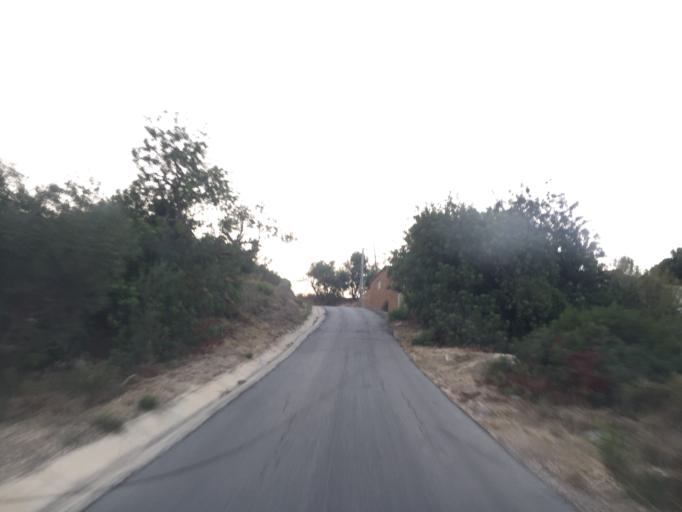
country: PT
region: Faro
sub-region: Loule
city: Almancil
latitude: 37.1037
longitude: -8.0168
